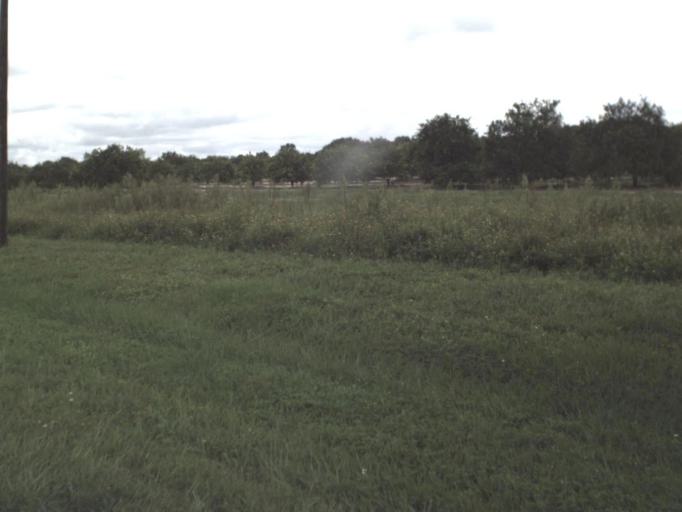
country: US
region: Florida
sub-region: Hillsborough County
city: Wimauma
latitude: 27.5813
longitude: -82.1875
